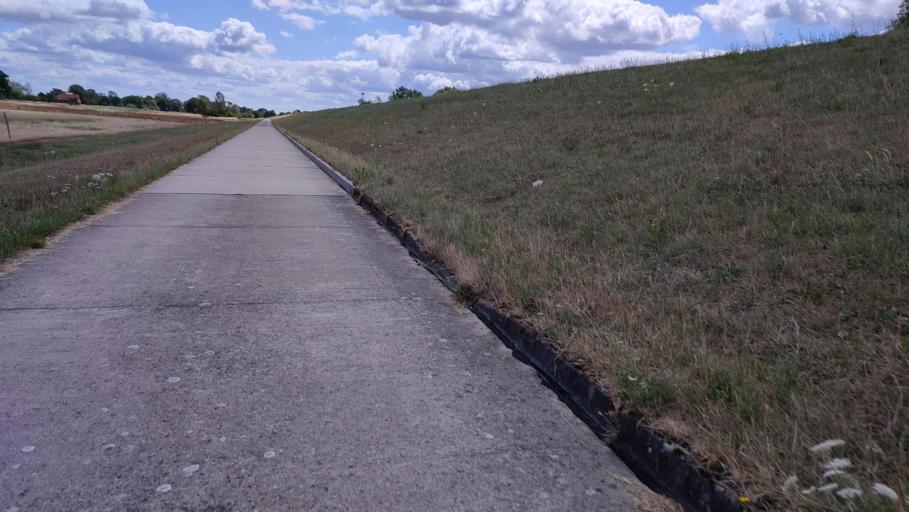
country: DE
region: Lower Saxony
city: Hitzacker
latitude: 53.1913
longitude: 10.9975
